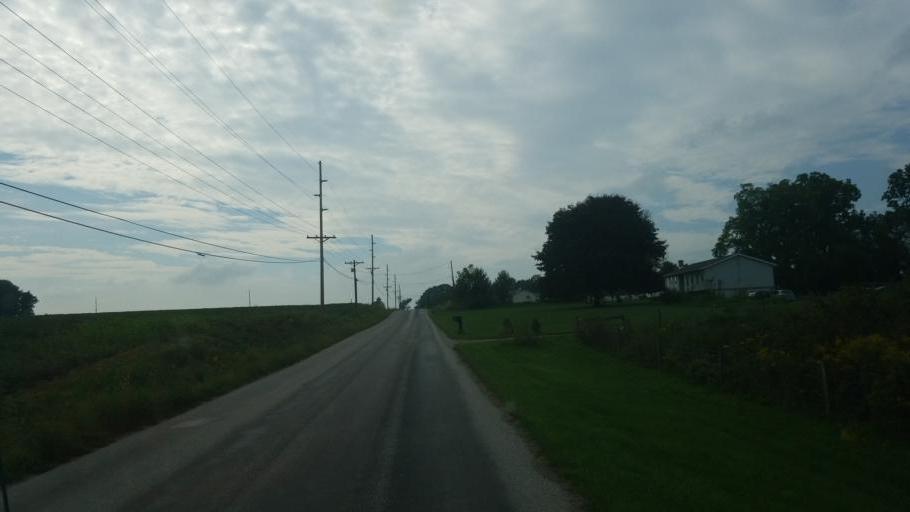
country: US
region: Ohio
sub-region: Wayne County
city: Wooster
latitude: 40.9013
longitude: -81.9779
